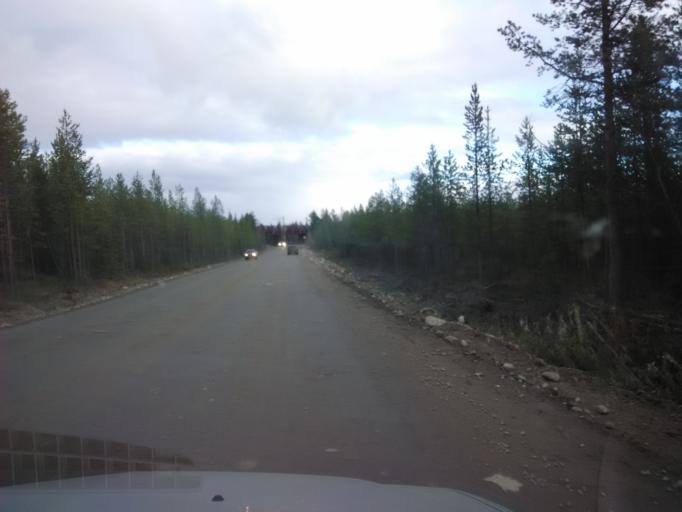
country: RU
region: Murmansk
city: Polyarnyye Zori
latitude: 67.3753
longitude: 32.5105
